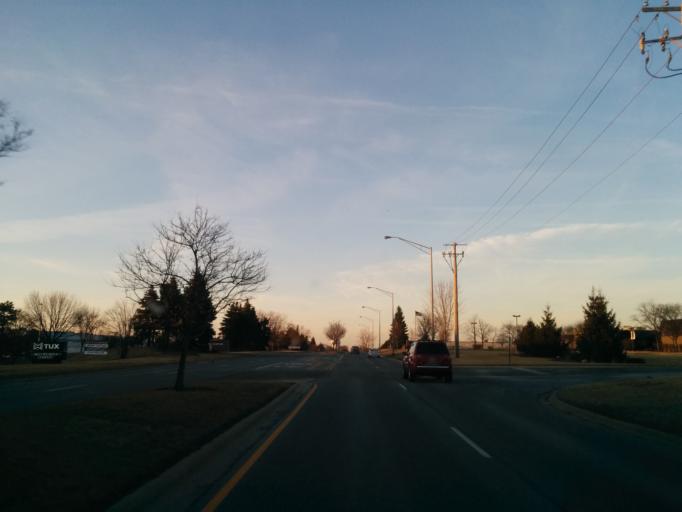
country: US
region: Illinois
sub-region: DuPage County
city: Glendale Heights
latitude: 41.9237
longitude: -88.0423
